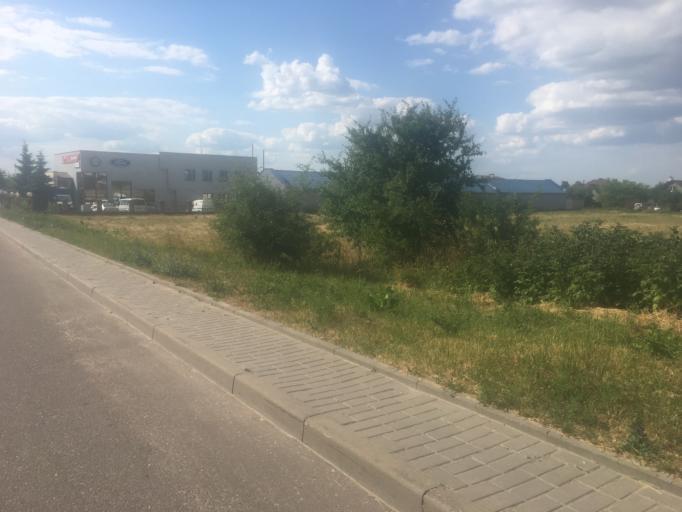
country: BY
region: Grodnenskaya
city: Hrodna
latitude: 53.6479
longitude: 23.8130
